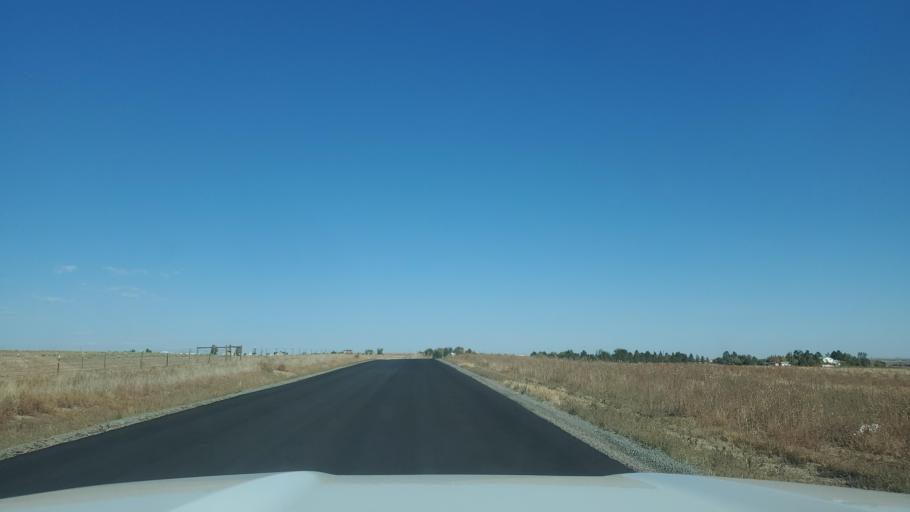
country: US
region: Colorado
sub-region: Adams County
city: Bennett
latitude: 39.7639
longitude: -104.3769
